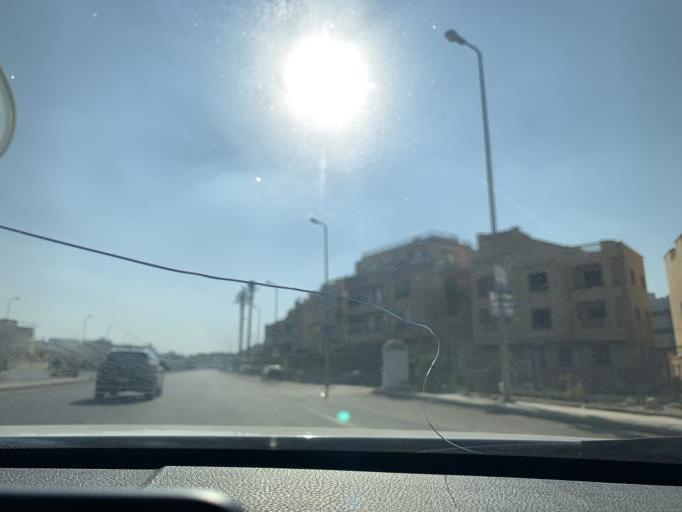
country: EG
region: Muhafazat al Qalyubiyah
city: Al Khankah
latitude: 30.0076
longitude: 31.4827
